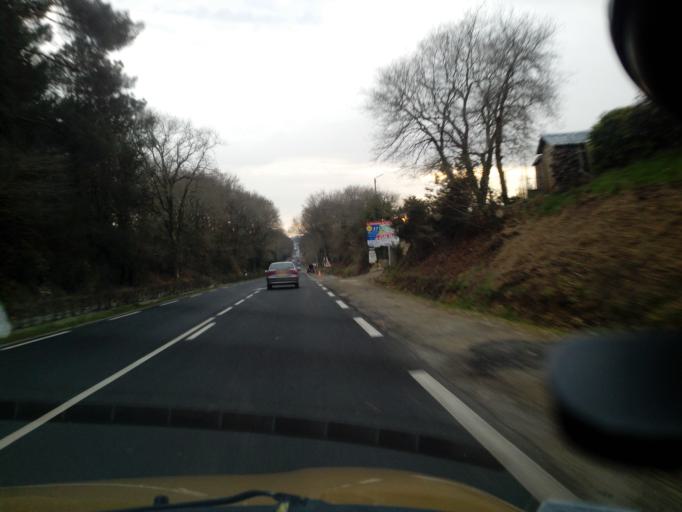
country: FR
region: Brittany
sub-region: Departement du Morbihan
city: Hennebont
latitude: 47.8121
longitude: -3.2500
